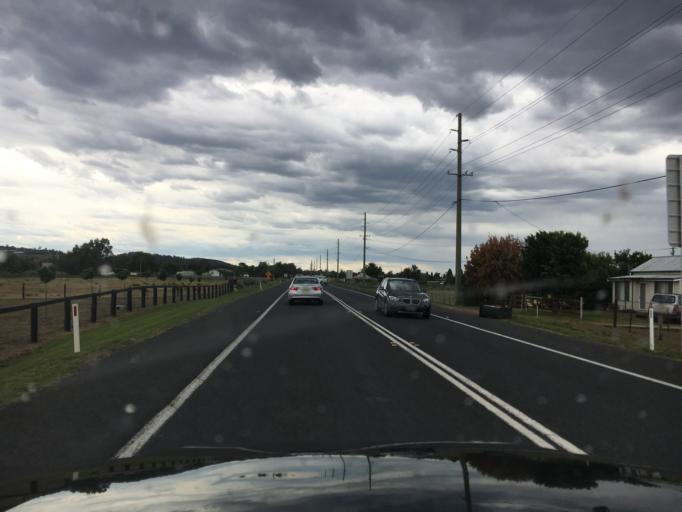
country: AU
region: New South Wales
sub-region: Muswellbrook
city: Muswellbrook
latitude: -32.1466
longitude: 150.8831
